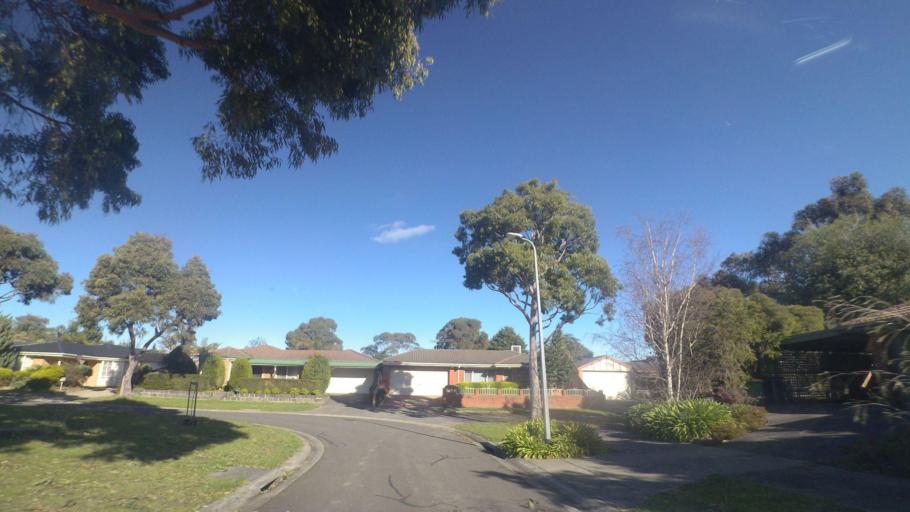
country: AU
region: Victoria
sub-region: Knox
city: Rowville
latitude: -37.9324
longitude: 145.2453
